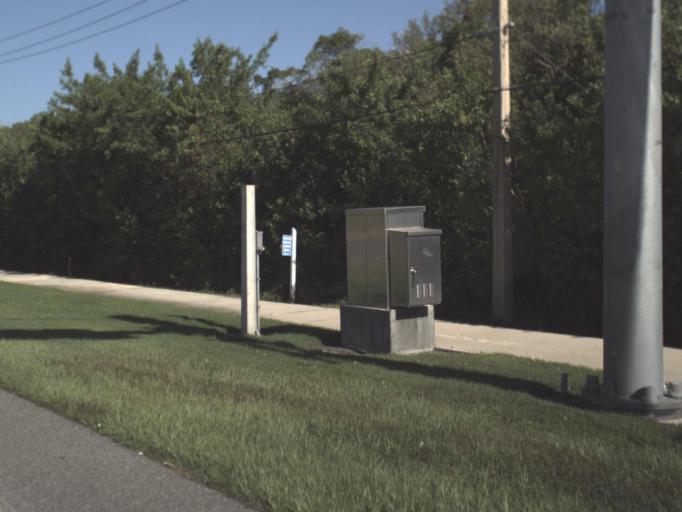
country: US
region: Florida
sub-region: Sarasota County
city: Siesta Key
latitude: 27.3365
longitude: -82.5865
